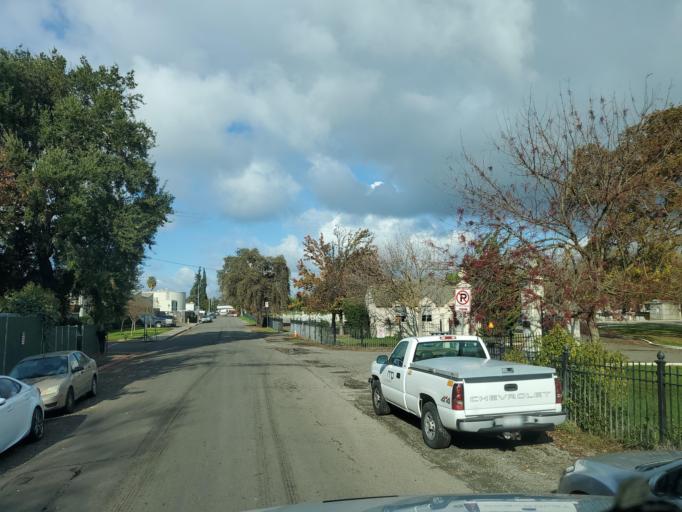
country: US
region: California
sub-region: San Joaquin County
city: Stockton
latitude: 37.9714
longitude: -121.2877
